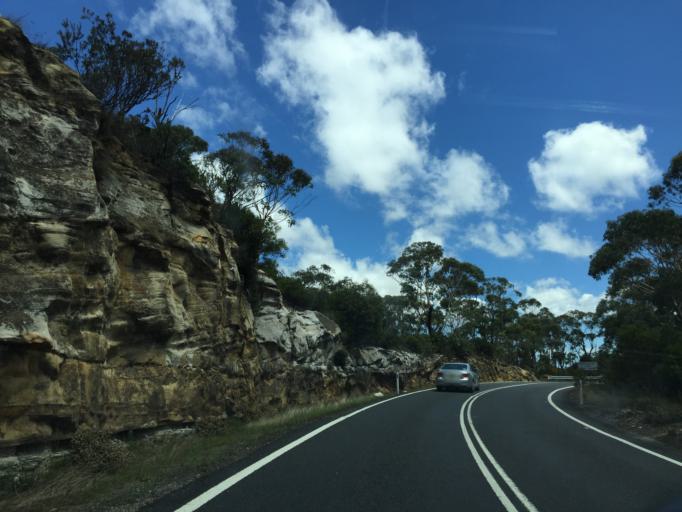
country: AU
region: New South Wales
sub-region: Blue Mountains Municipality
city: Blackheath
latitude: -33.5545
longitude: 150.3787
